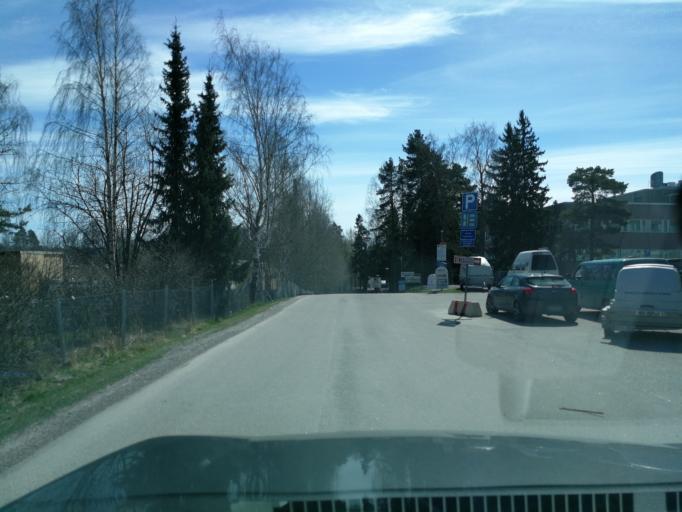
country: FI
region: Uusimaa
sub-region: Helsinki
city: Koukkuniemi
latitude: 60.1567
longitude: 24.7093
